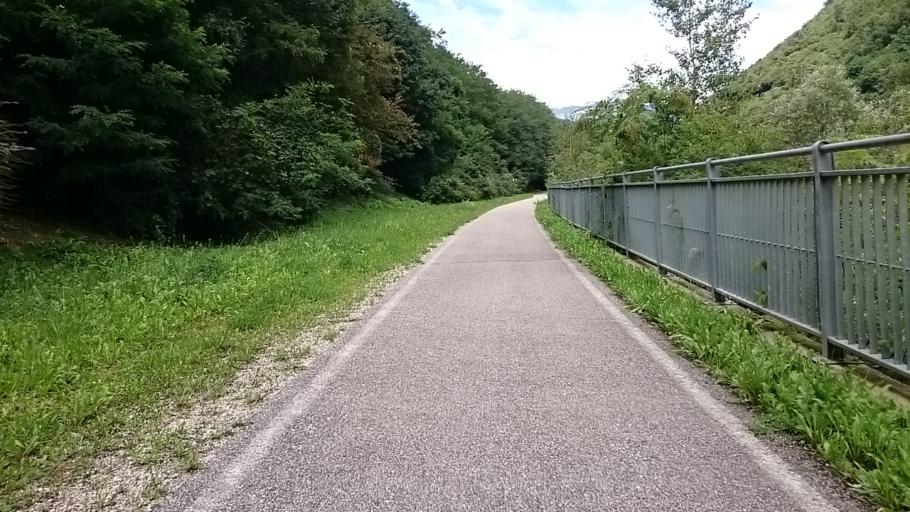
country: IT
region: Trentino-Alto Adige
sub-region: Bolzano
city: Ponte Gardena
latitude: 46.5777
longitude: 11.5223
